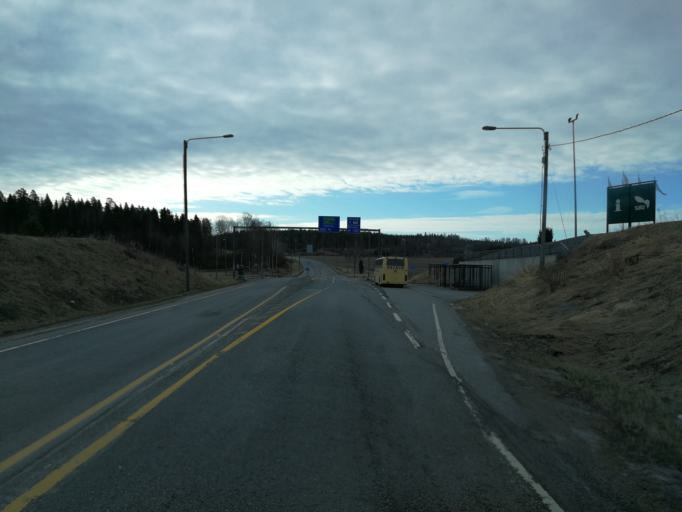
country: FI
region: Varsinais-Suomi
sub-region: Salo
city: Muurla
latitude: 60.3746
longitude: 23.3115
